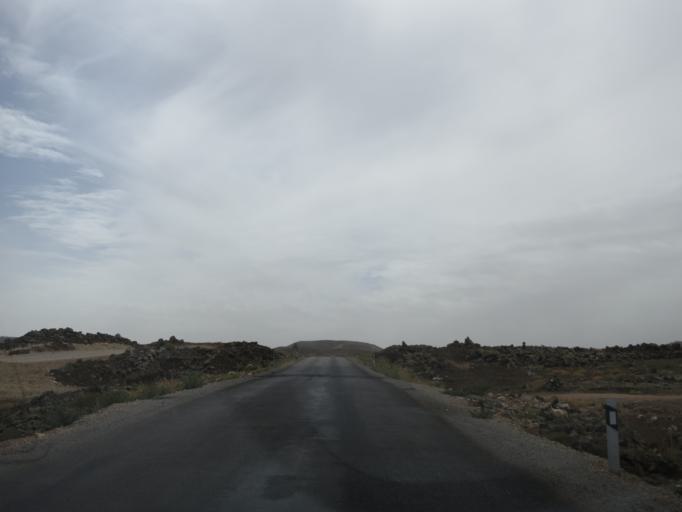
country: MA
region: Meknes-Tafilalet
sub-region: Khenifra
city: Itzer
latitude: 33.1270
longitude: -5.0337
